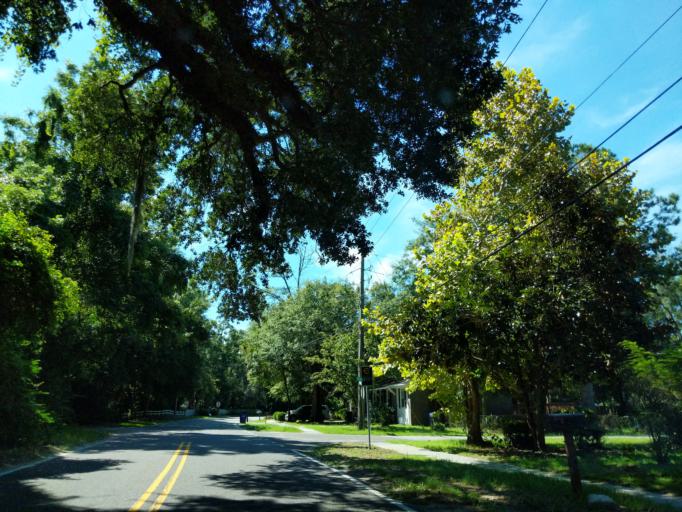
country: US
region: South Carolina
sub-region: Charleston County
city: Folly Beach
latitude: 32.7166
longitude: -79.9569
